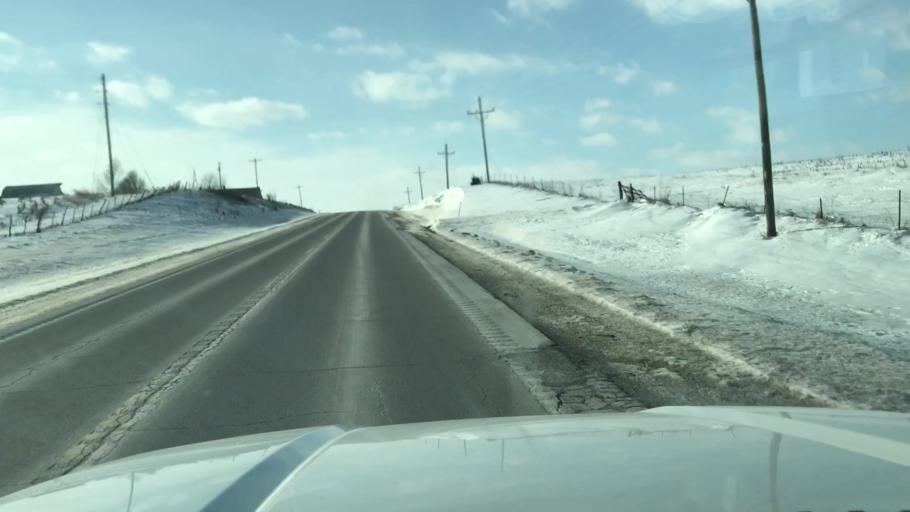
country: US
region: Missouri
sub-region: Nodaway County
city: Maryville
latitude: 40.3441
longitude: -94.7487
